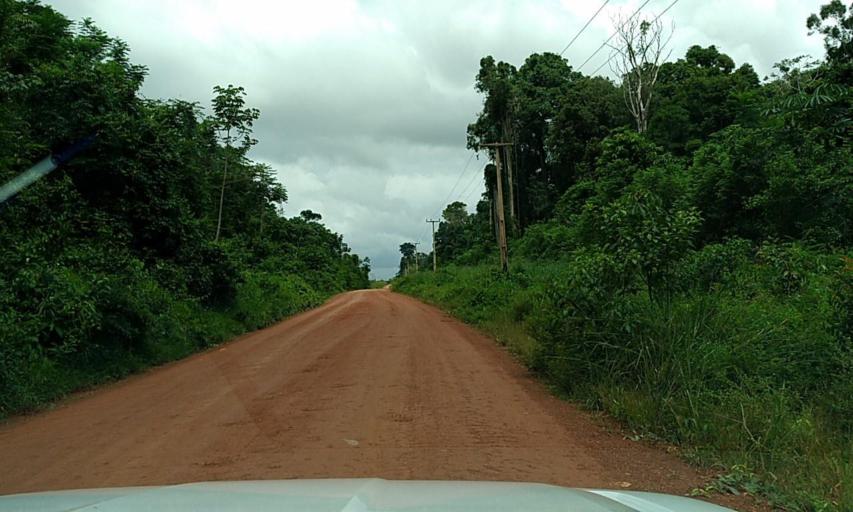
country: BR
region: Para
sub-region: Senador Jose Porfirio
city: Senador Jose Porfirio
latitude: -2.6755
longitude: -51.8343
